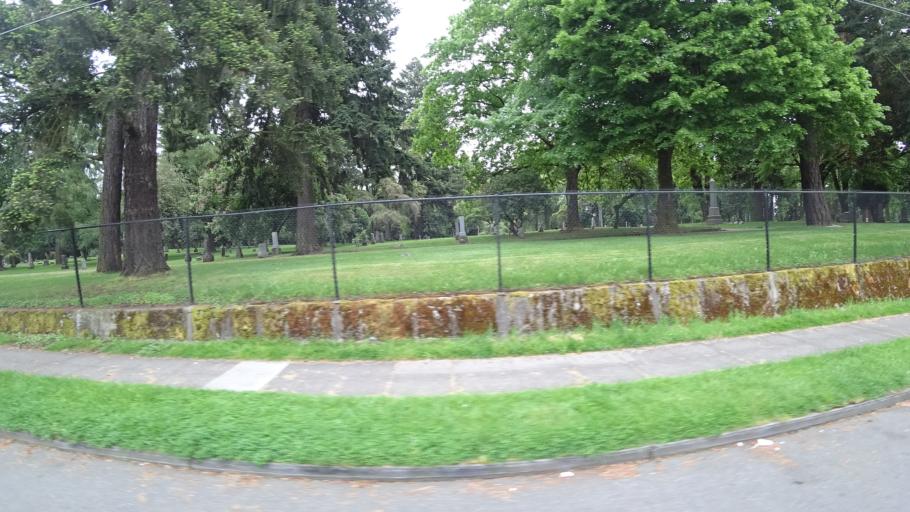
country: US
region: Oregon
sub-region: Multnomah County
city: Portland
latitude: 45.5193
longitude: -122.6418
